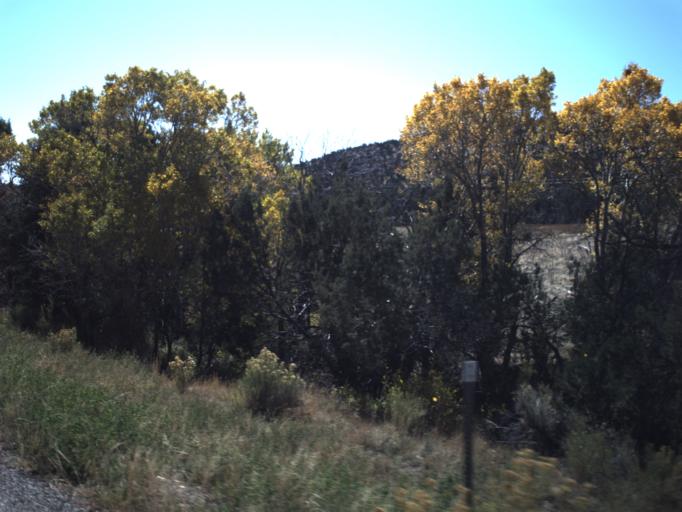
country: US
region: Utah
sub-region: Wayne County
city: Loa
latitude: 37.9304
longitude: -111.4293
